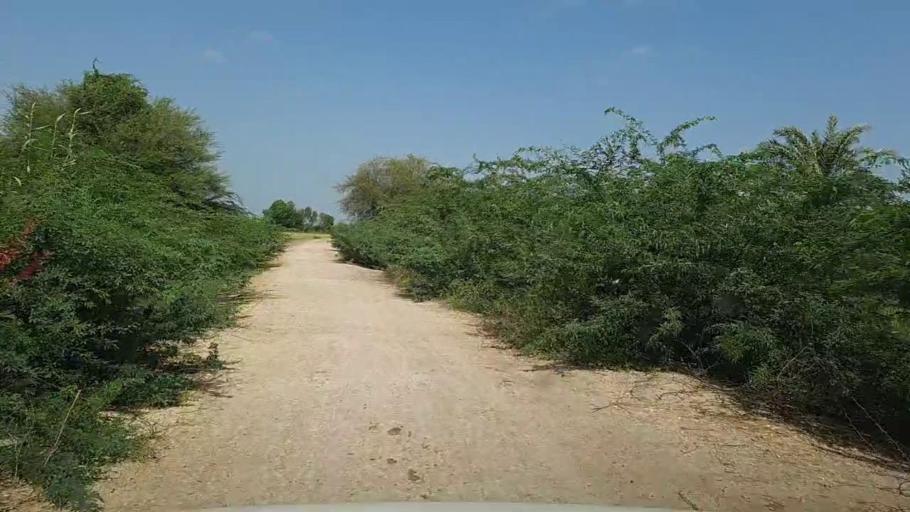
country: PK
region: Sindh
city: Kario
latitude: 24.8356
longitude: 68.7136
